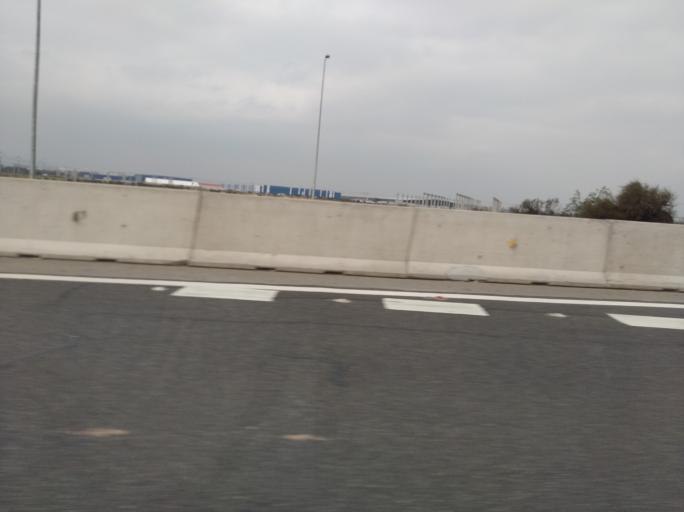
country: CL
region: Santiago Metropolitan
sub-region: Provincia de Santiago
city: Lo Prado
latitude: -33.4319
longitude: -70.8095
